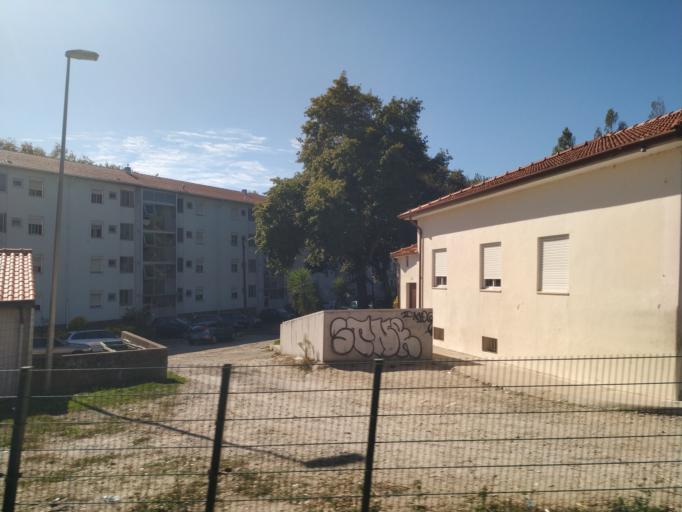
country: PT
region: Porto
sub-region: Matosinhos
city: Senhora da Hora
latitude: 41.1684
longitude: -8.6384
